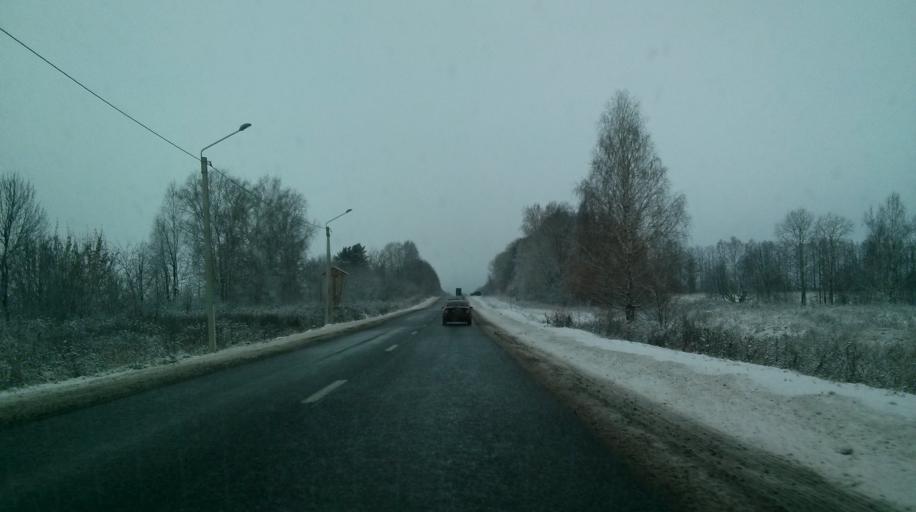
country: RU
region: Nizjnij Novgorod
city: Bogorodsk
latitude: 56.0606
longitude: 43.4188
